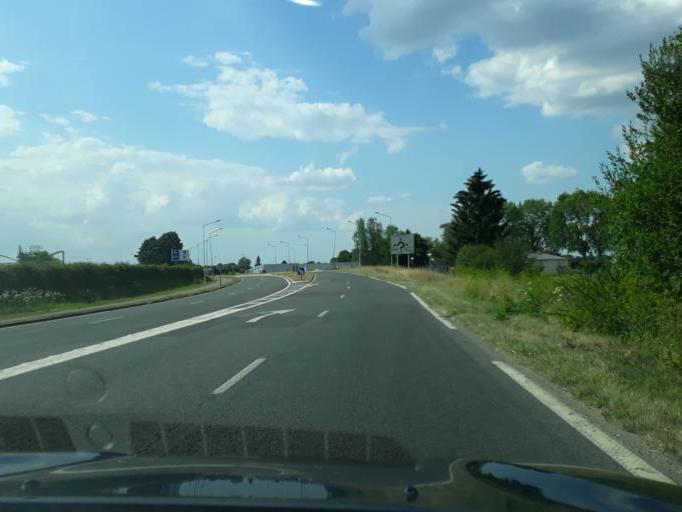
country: FR
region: Bourgogne
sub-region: Departement de la Nievre
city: Marzy
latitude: 46.9973
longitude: 3.1102
